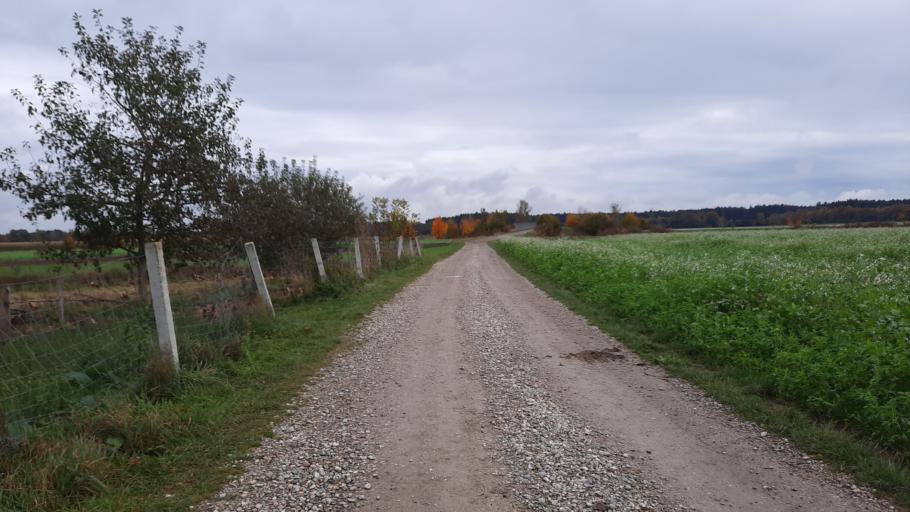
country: DE
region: Bavaria
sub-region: Upper Bavaria
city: Zorneding
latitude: 48.0801
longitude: 11.8328
